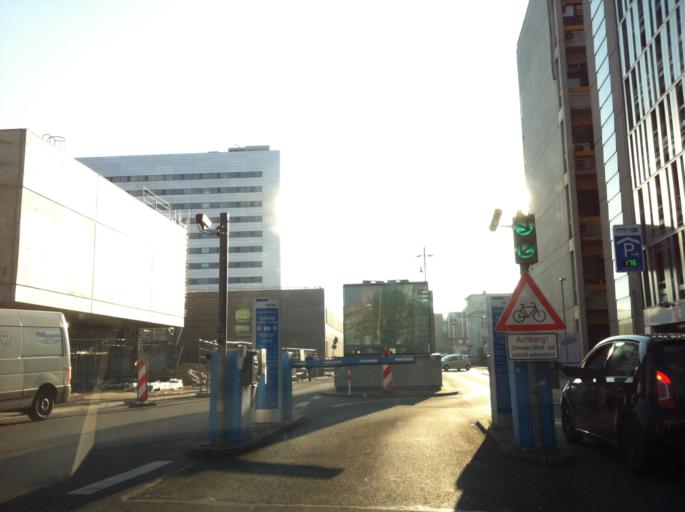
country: DE
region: Hesse
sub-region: Regierungsbezirk Darmstadt
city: Frankfurt am Main
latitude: 50.0954
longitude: 8.6592
